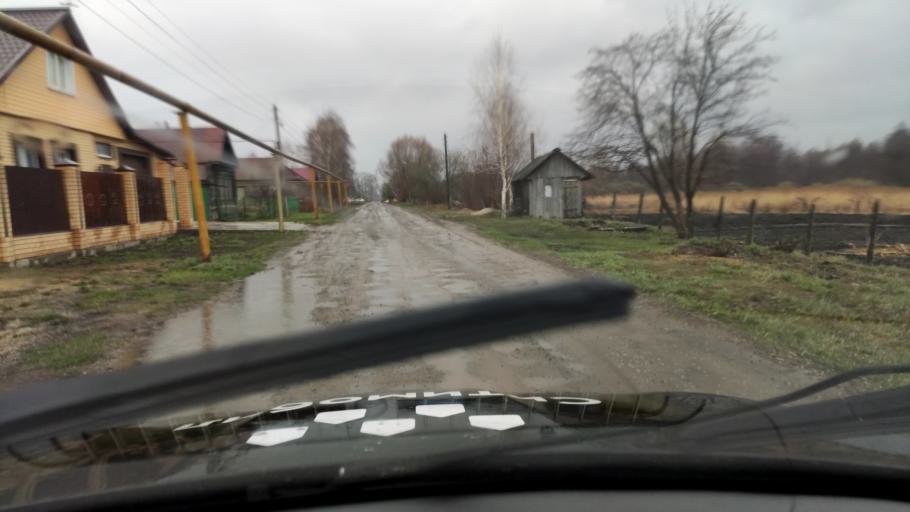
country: RU
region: Samara
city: Balasheyka
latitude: 53.2303
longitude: 48.2445
